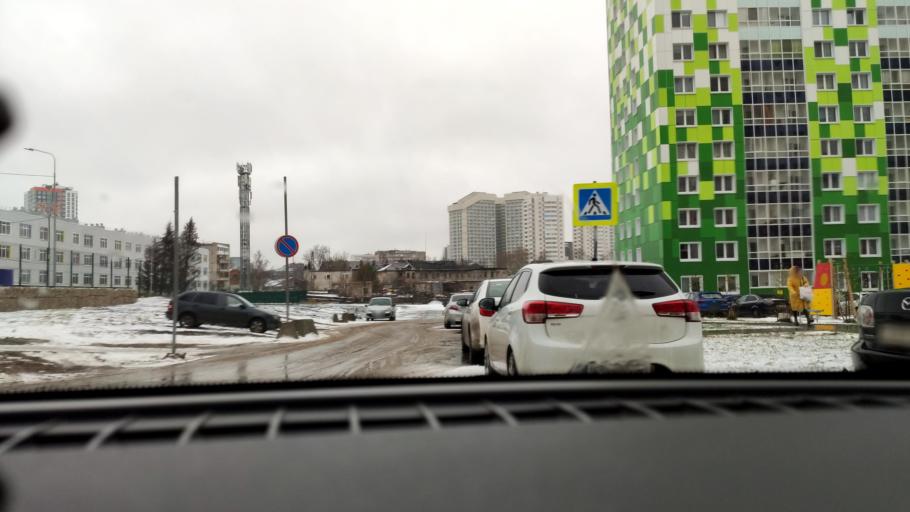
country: RU
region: Perm
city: Perm
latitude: 57.9910
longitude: 56.2665
